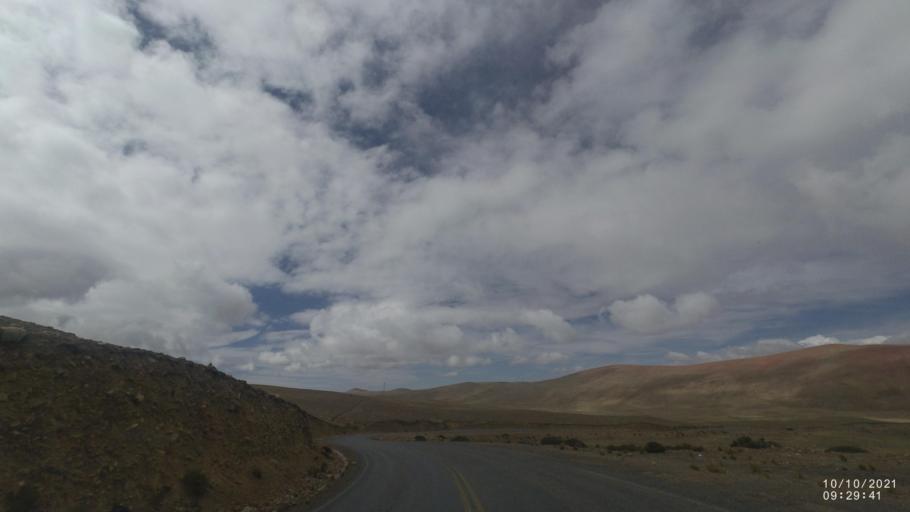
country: BO
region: La Paz
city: Quime
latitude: -17.1155
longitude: -67.3264
